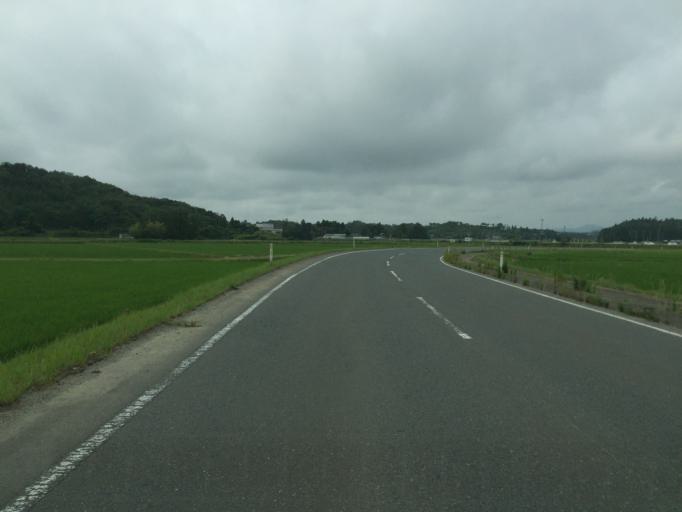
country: JP
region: Miyagi
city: Marumori
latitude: 37.7639
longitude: 140.9499
